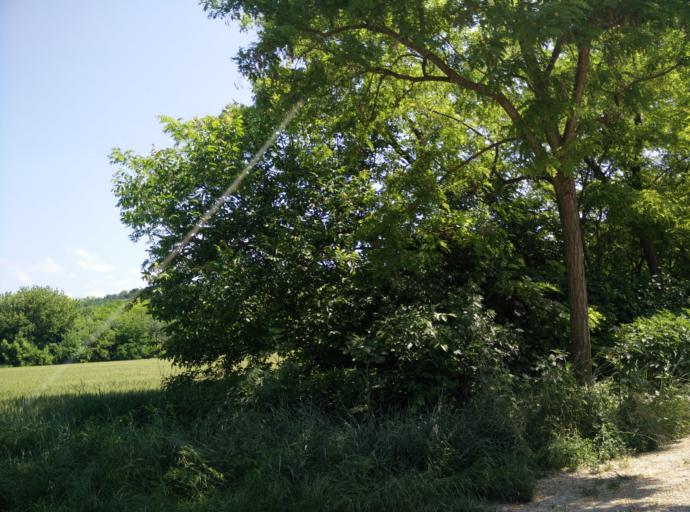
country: HU
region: Pest
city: Biatorbagy
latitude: 47.4577
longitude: 18.8255
